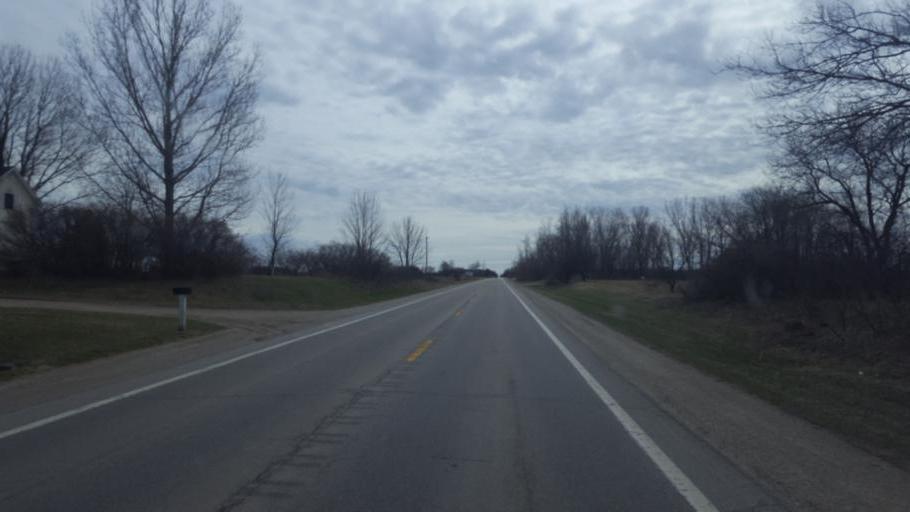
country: US
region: Michigan
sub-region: Isabella County
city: Lake Isabella
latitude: 43.7063
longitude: -85.1467
